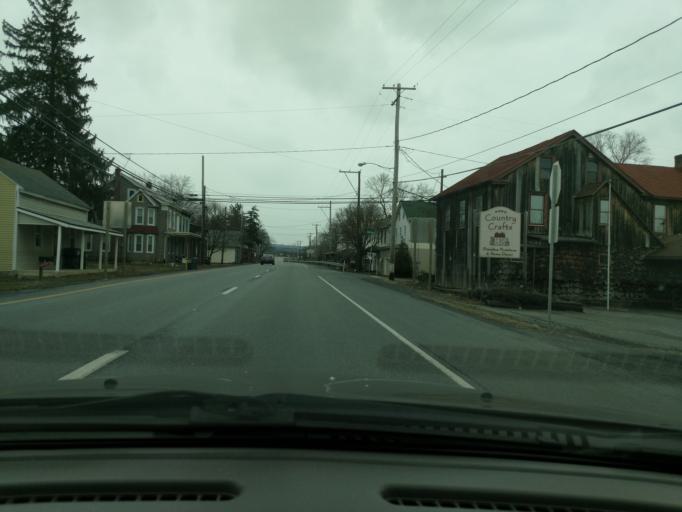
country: US
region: Pennsylvania
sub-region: Schuylkill County
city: Orwigsburg
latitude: 40.6251
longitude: -76.0607
